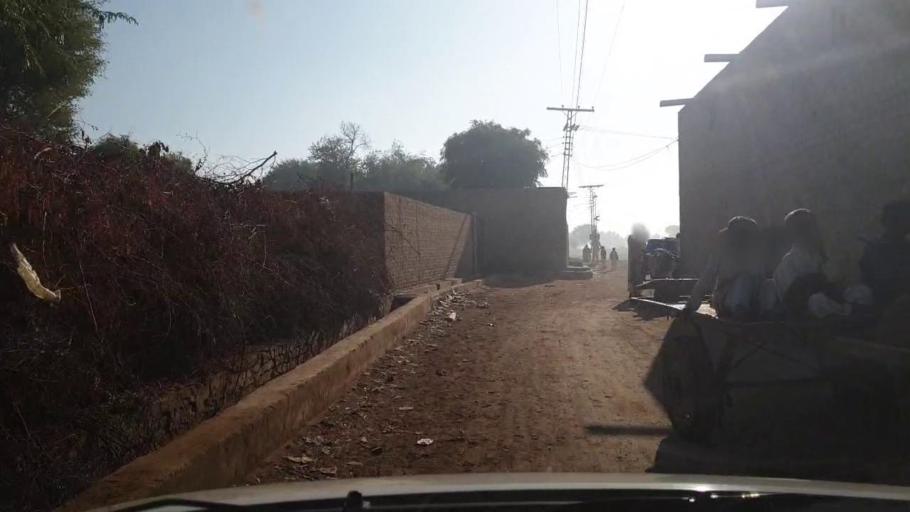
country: PK
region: Sindh
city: Dadu
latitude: 26.6821
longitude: 67.7806
